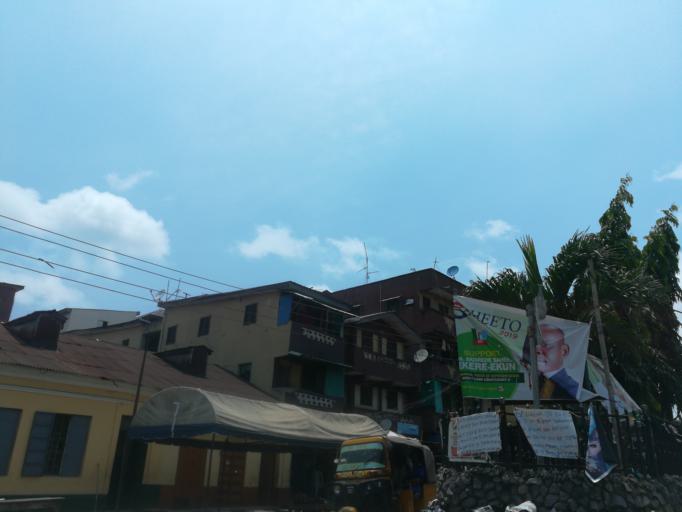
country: NG
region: Lagos
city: Lagos
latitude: 6.4527
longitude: 3.3983
